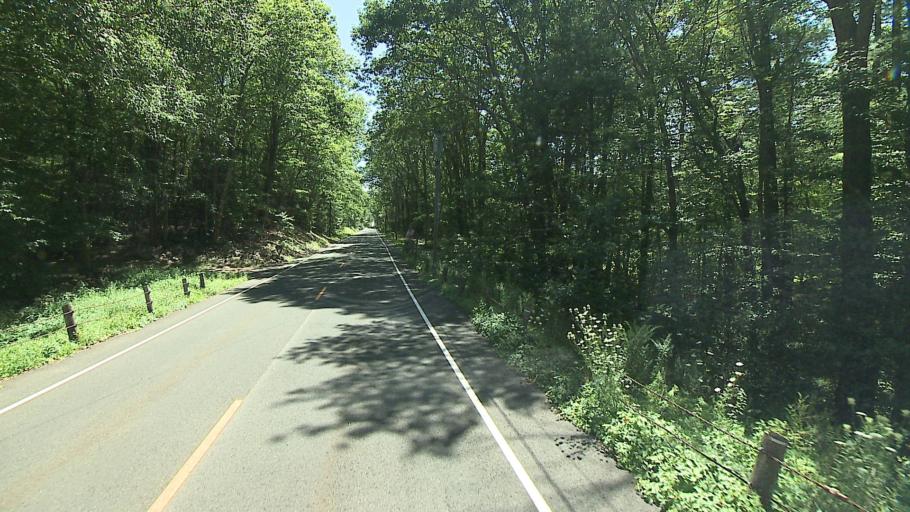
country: US
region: Connecticut
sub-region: Litchfield County
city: New Hartford Center
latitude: 41.9451
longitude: -72.9728
